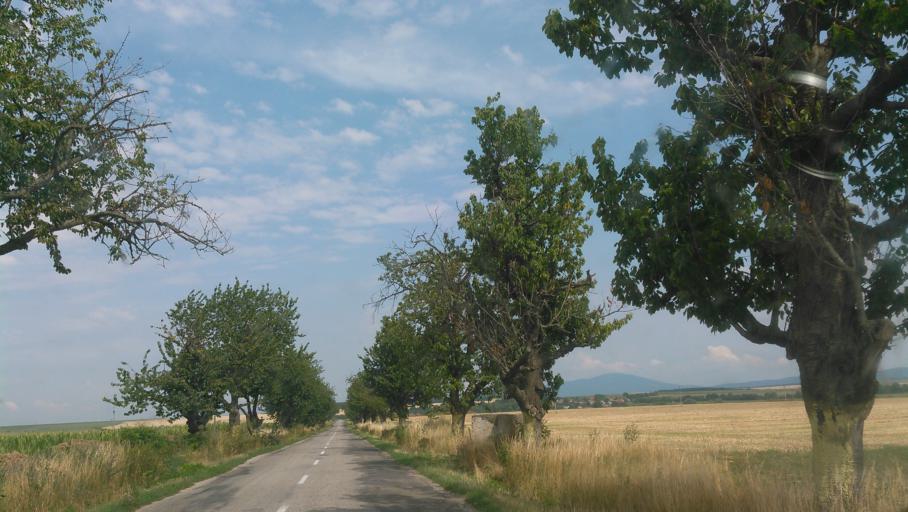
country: SK
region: Trnavsky
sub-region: Okres Trnava
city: Piestany
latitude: 48.5028
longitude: 17.9914
